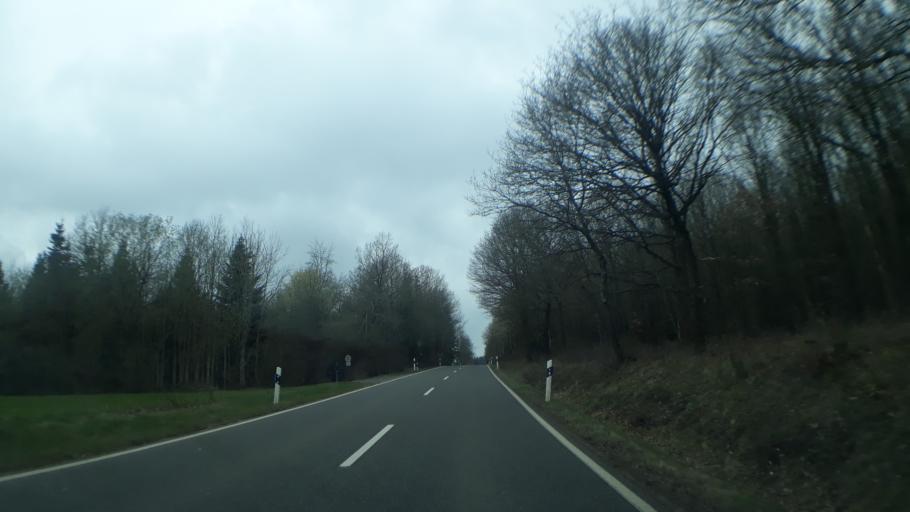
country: DE
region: North Rhine-Westphalia
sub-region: Regierungsbezirk Koln
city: Schleiden
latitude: 50.5254
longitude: 6.5142
